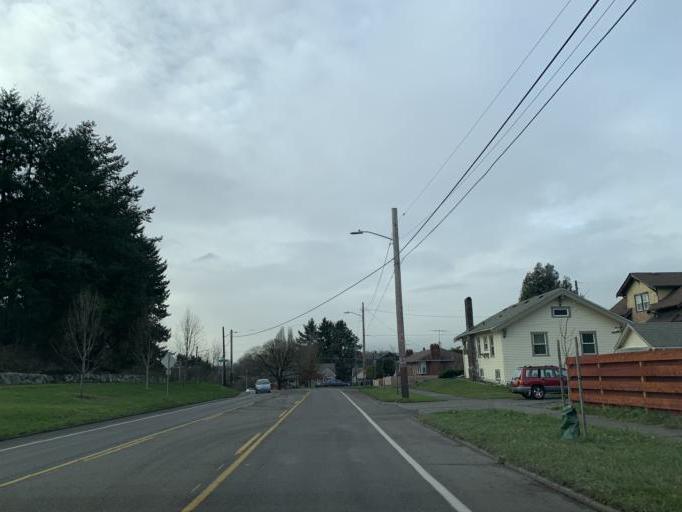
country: US
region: Washington
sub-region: King County
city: Seattle
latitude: 47.5720
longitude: -122.3105
